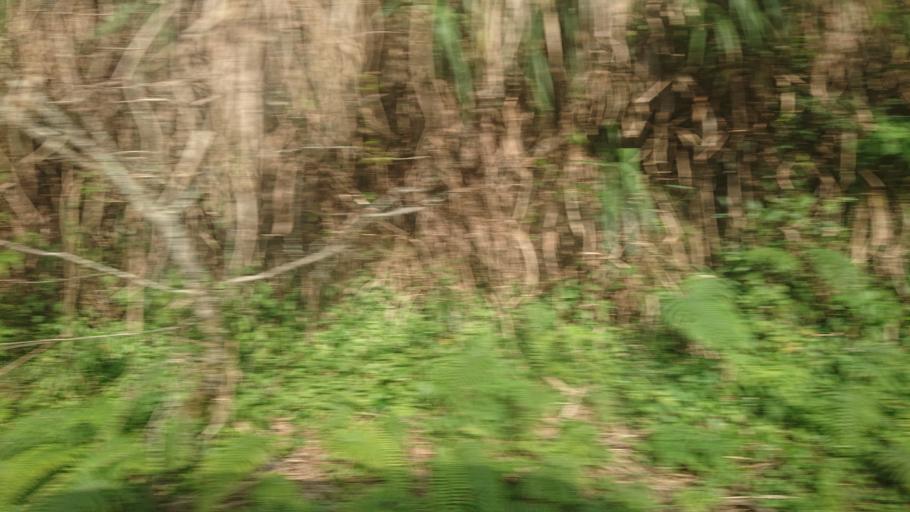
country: TW
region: Taiwan
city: Lugu
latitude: 23.5013
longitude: 120.7828
